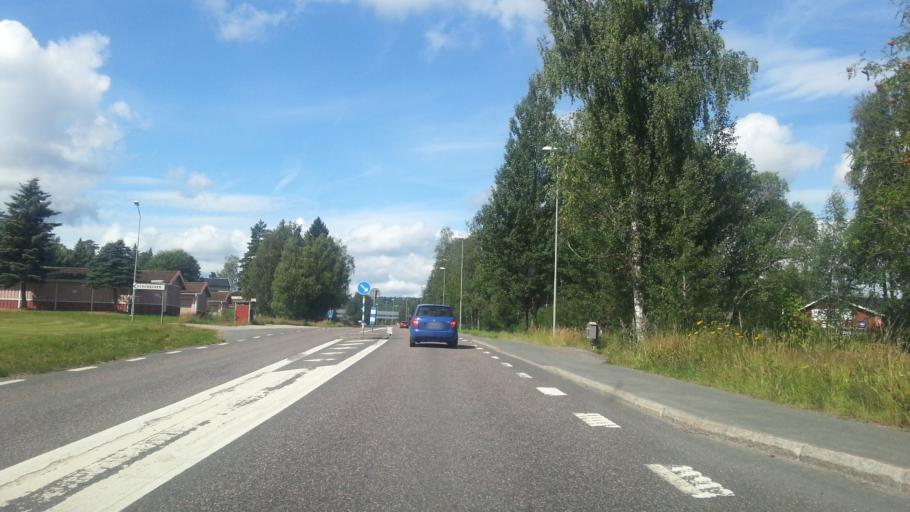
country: SE
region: Dalarna
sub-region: Ludvika Kommun
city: Grangesberg
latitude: 60.0791
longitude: 15.0246
